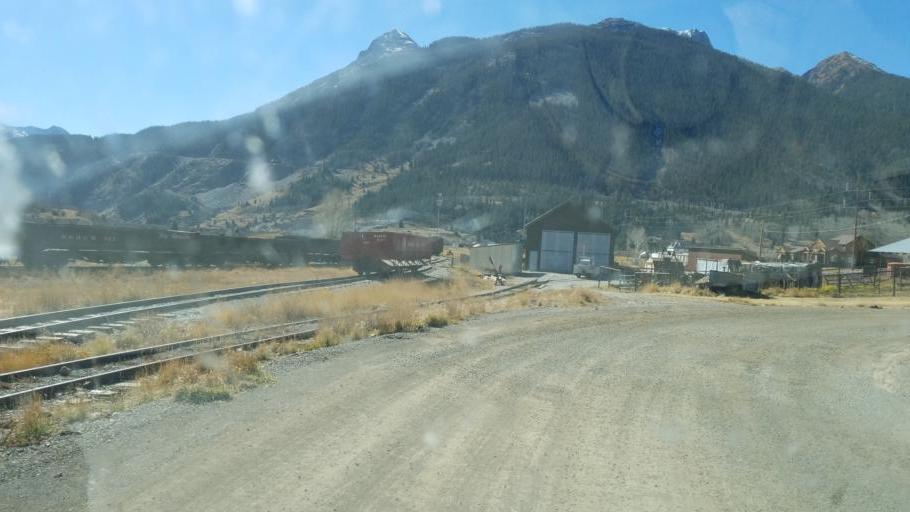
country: US
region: Colorado
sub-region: San Juan County
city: Silverton
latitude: 37.8084
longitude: -107.6640
